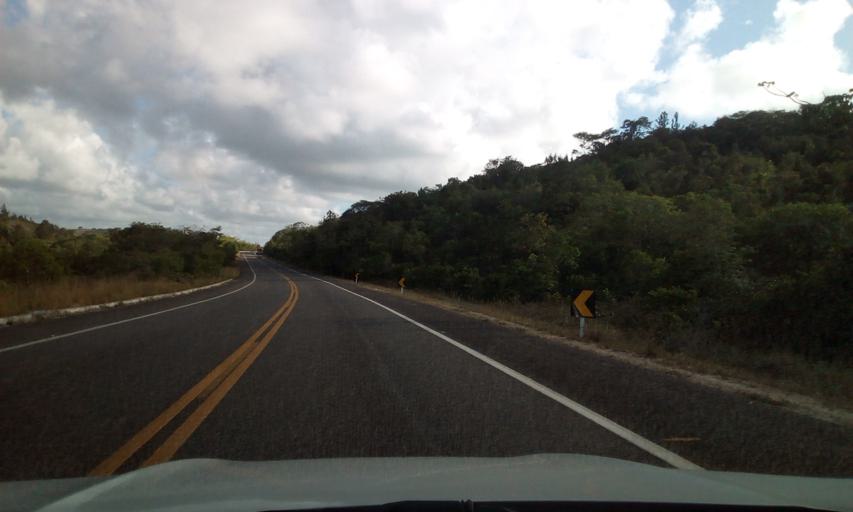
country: BR
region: Bahia
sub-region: Conde
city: Conde
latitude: -12.0726
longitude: -37.7501
